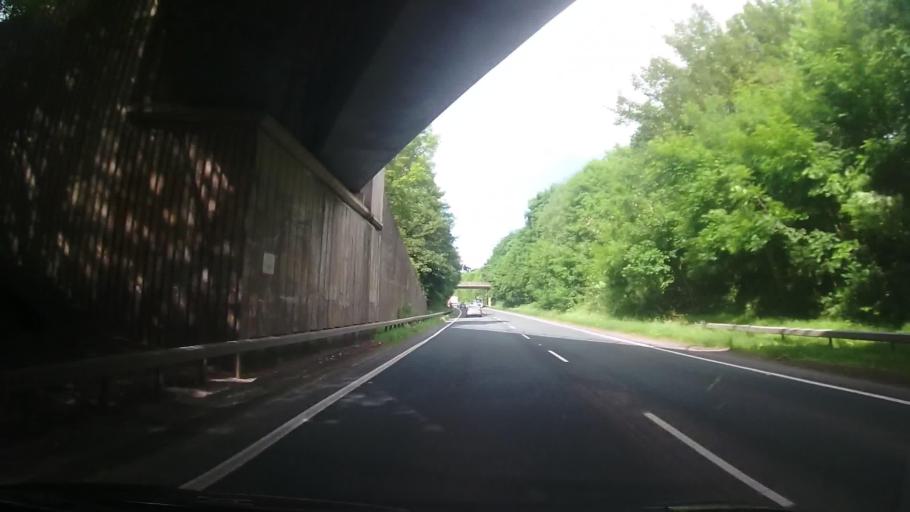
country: GB
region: England
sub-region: Shropshire
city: Ludlow
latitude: 52.3552
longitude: -2.7030
